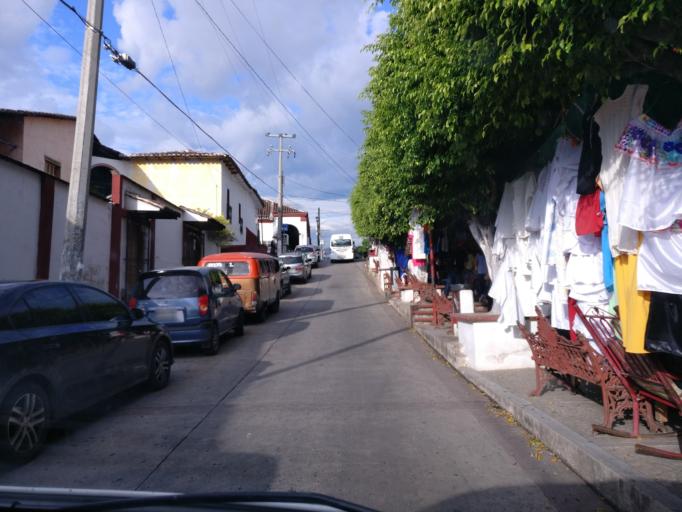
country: MX
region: Chiapas
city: Chiapa de Corzo
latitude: 16.7077
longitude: -93.0184
